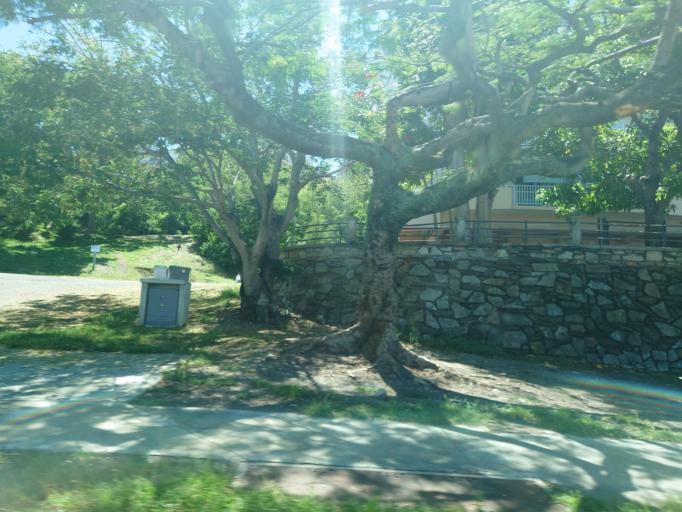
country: NC
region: South Province
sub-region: Noumea
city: Noumea
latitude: -22.2744
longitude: 166.4494
